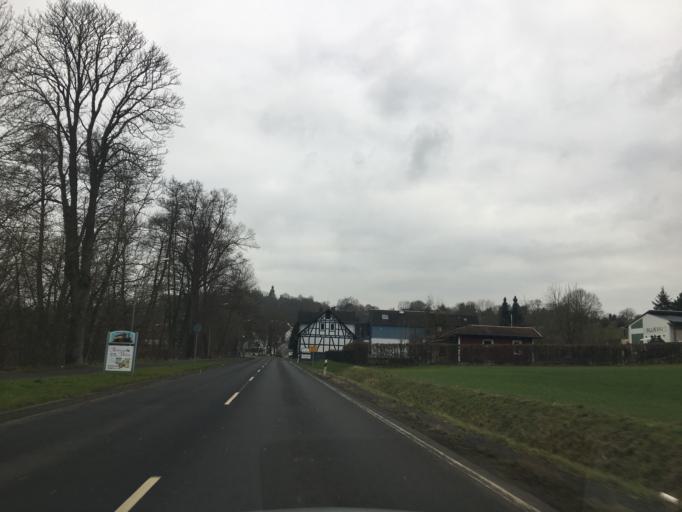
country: DE
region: Hesse
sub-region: Regierungsbezirk Giessen
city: Alsfeld
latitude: 50.7387
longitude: 9.2718
